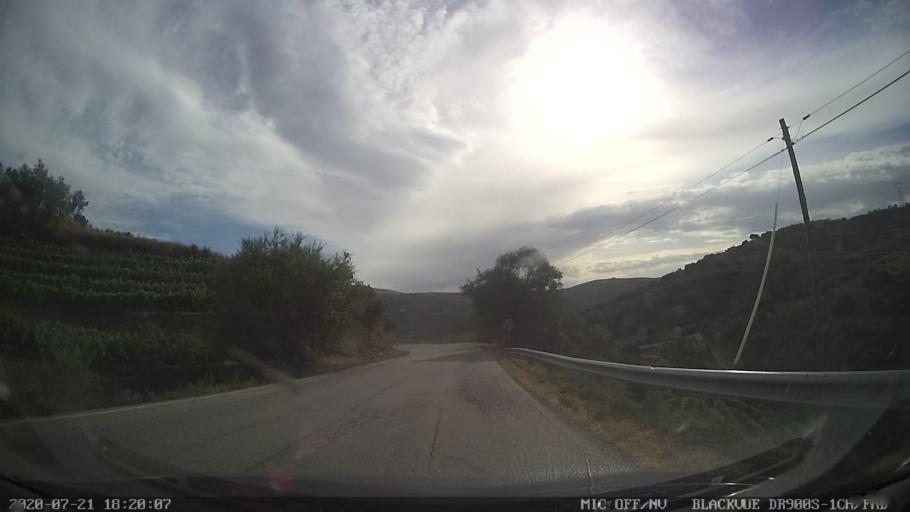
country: PT
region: Guarda
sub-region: Vila Nova de Foz Coa
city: Custoias
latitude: 41.0893
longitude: -7.3781
